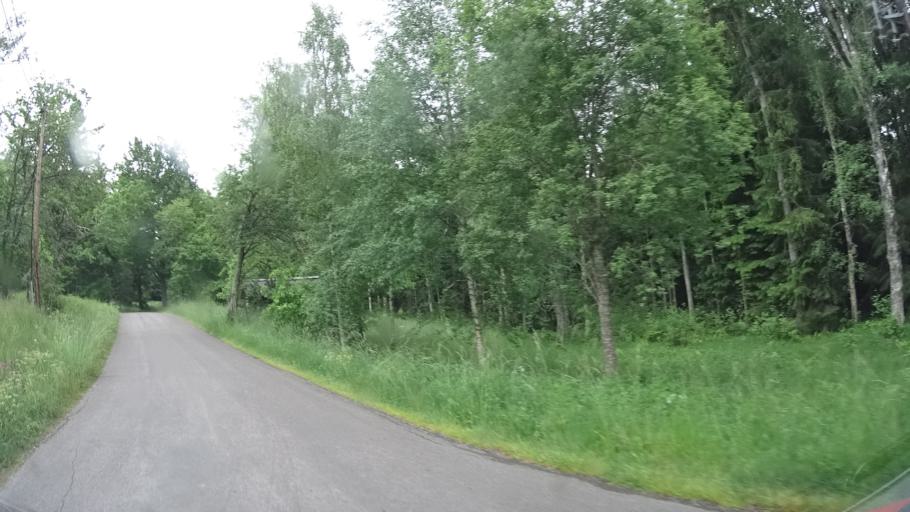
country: SE
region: Joenkoeping
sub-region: Eksjo Kommun
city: Mariannelund
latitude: 57.6850
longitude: 15.5691
